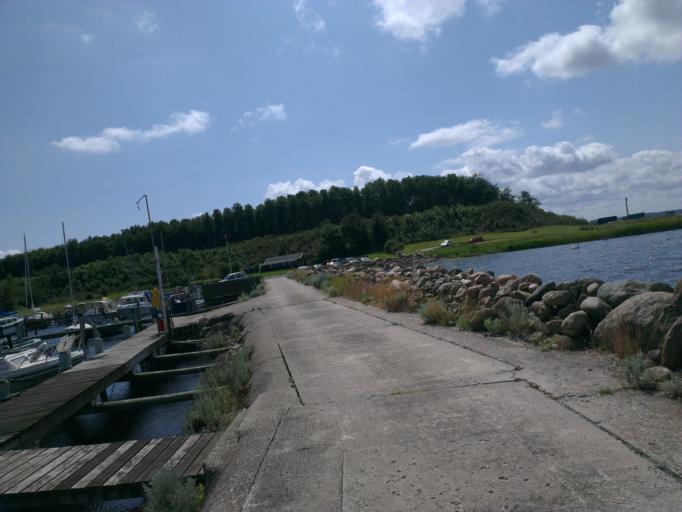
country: DK
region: Zealand
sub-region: Lejre Kommune
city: Ejby
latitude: 55.7570
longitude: 11.8503
